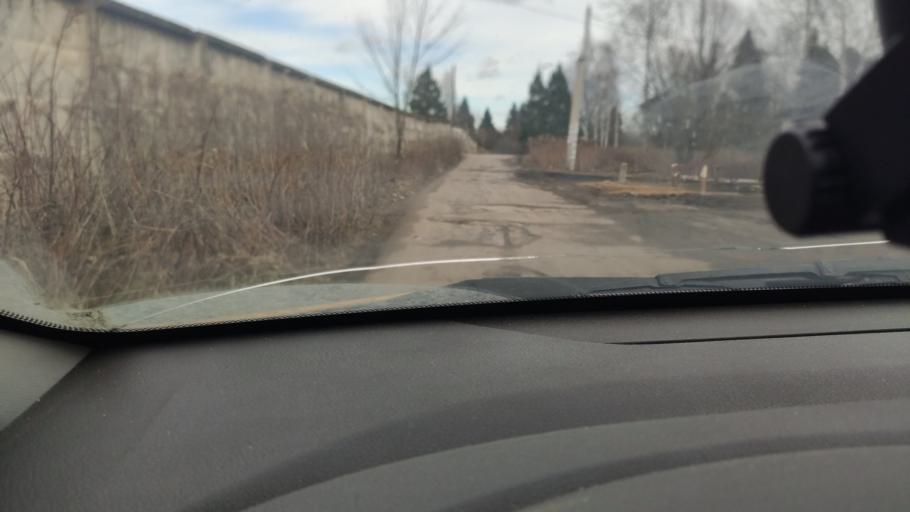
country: RU
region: Moskovskaya
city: Chupryakovo
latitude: 55.5834
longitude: 36.6221
